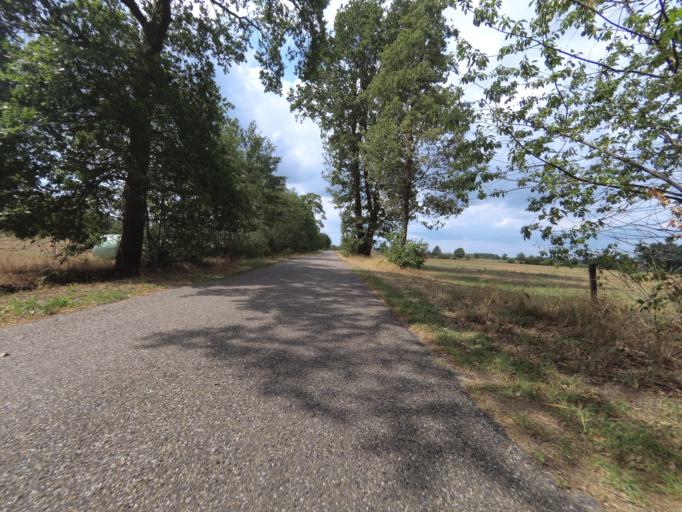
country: NL
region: Overijssel
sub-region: Gemeente Haaksbergen
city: Haaksbergen
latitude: 52.1379
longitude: 6.7741
